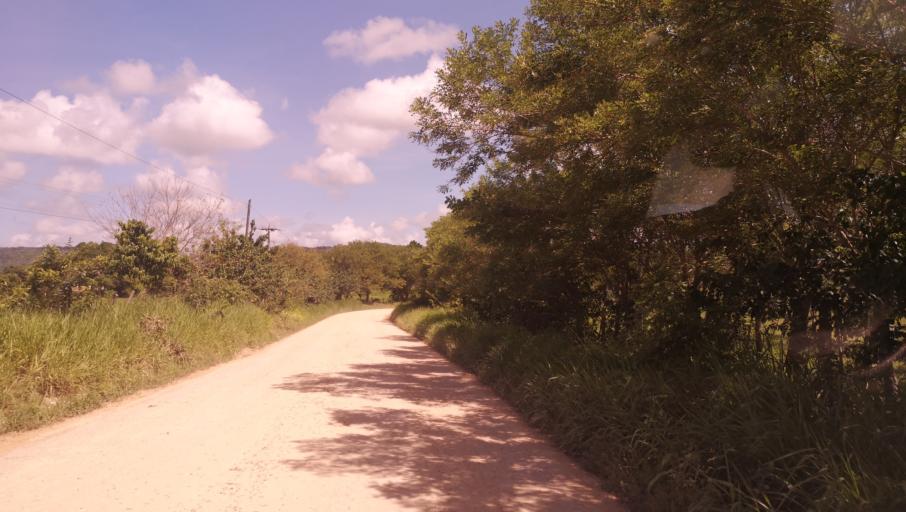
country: GT
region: Peten
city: Melchor de Mencos
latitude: 17.0163
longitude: -89.2439
